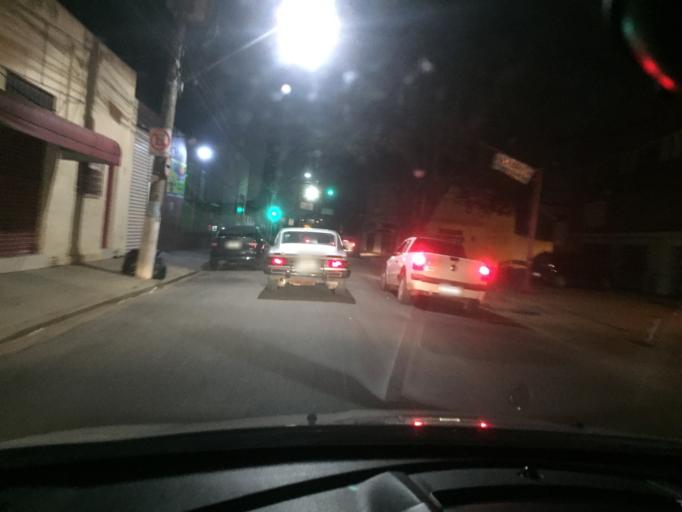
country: BR
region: Sao Paulo
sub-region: Jundiai
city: Jundiai
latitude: -23.2042
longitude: -46.8671
